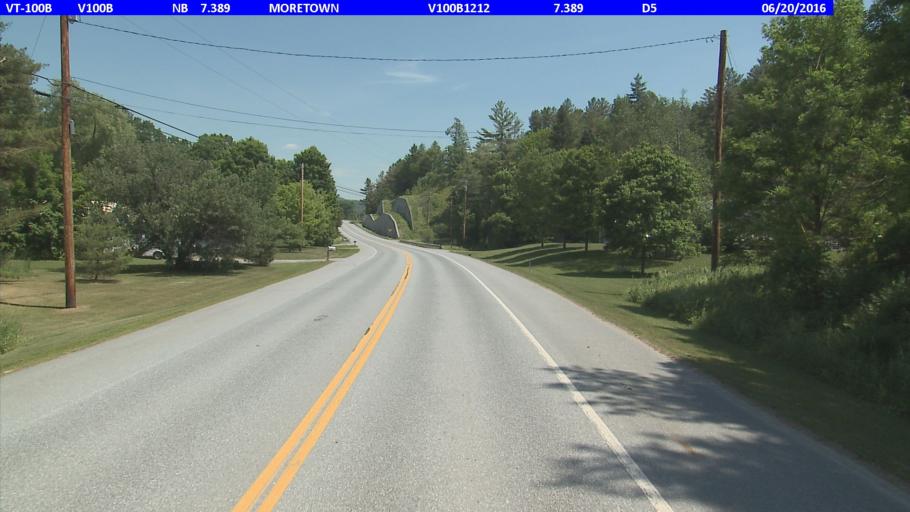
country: US
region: Vermont
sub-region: Washington County
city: Waterbury
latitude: 44.2925
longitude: -72.6879
